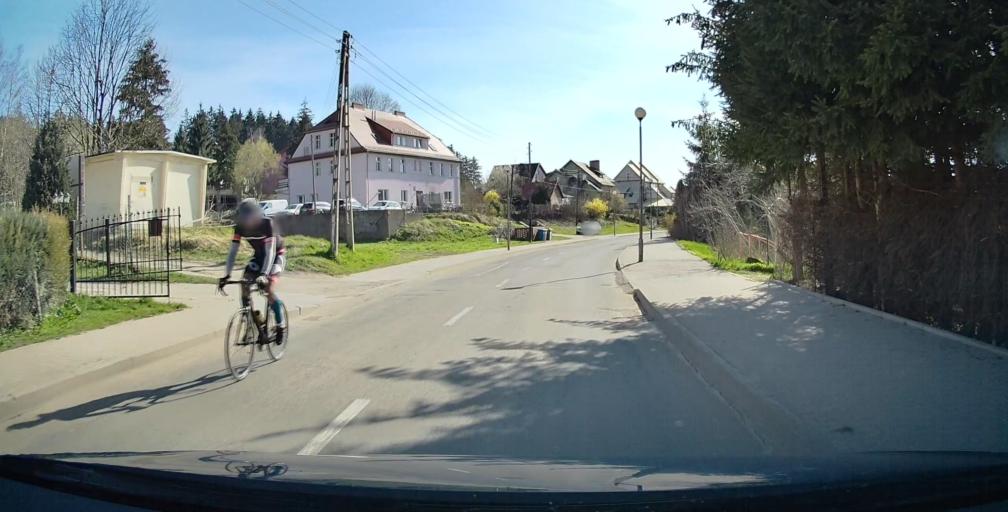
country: PL
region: Lower Silesian Voivodeship
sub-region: Powiat klodzki
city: Kudowa-Zdroj
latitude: 50.4441
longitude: 16.2538
